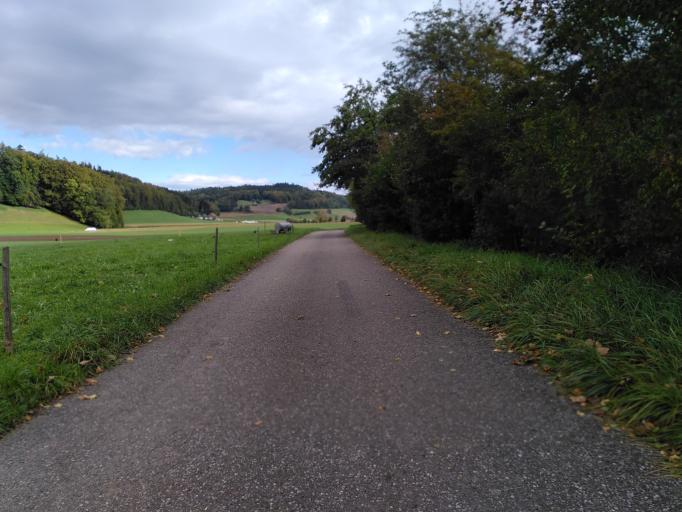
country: CH
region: Bern
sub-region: Emmental District
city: Wynigen
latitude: 47.1194
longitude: 7.6702
